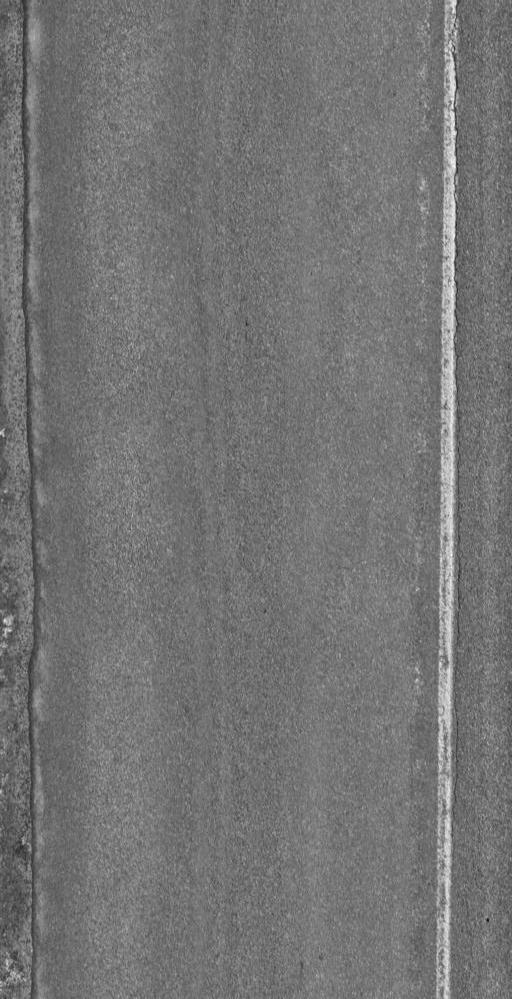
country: US
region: Vermont
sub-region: Chittenden County
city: South Burlington
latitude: 44.4142
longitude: -73.1380
